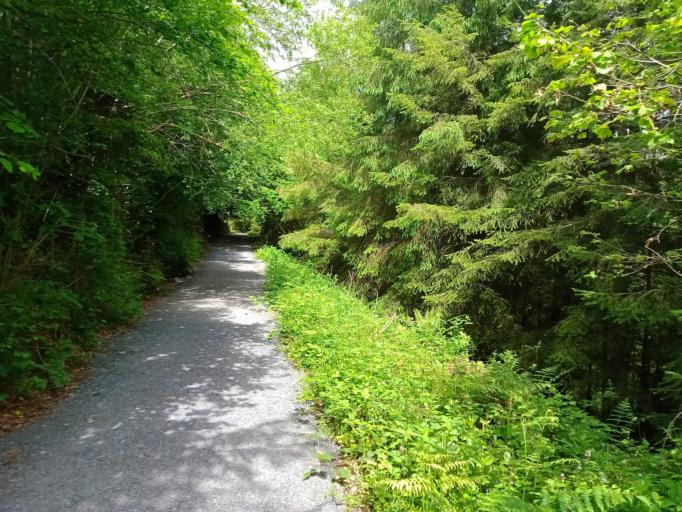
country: IE
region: Leinster
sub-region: Kilkenny
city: Thomastown
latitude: 52.4766
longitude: -7.0472
